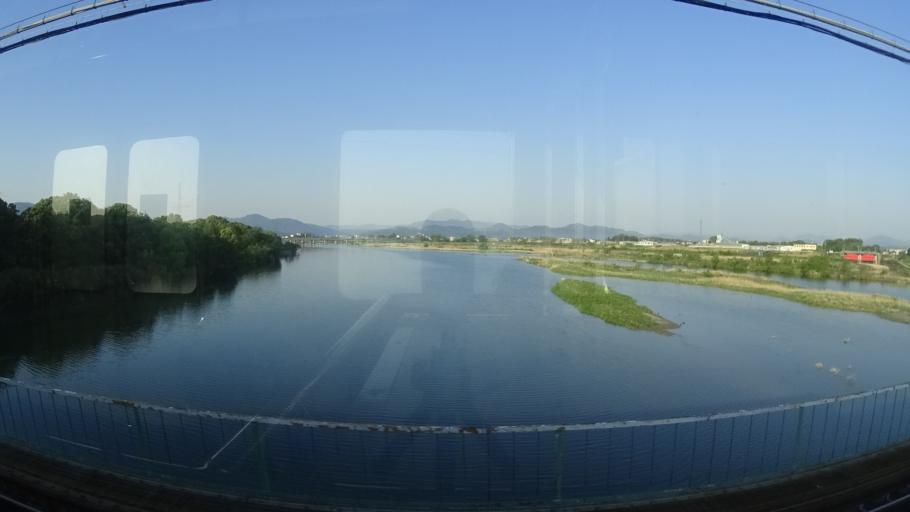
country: JP
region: Mie
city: Ise
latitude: 34.5093
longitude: 136.6895
